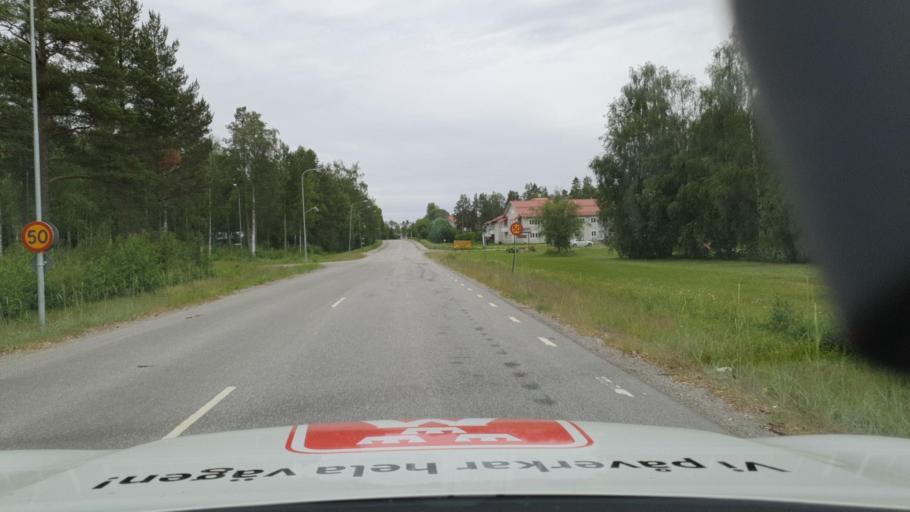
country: SE
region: Vaesterbotten
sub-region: Nordmalings Kommun
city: Nordmaling
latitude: 63.5446
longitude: 19.4381
